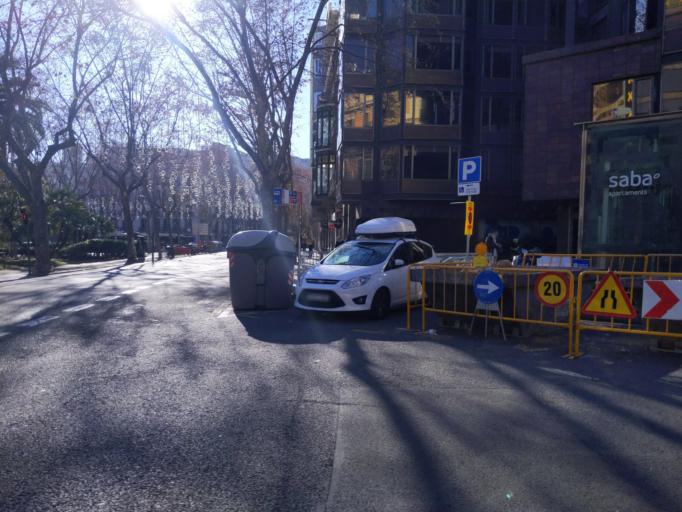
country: ES
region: Catalonia
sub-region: Provincia de Barcelona
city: Ciutat Vella
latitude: 41.3897
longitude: 2.1734
